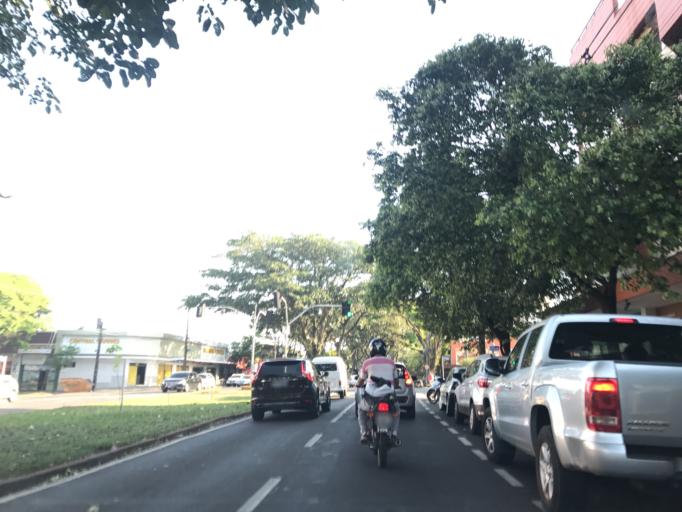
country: BR
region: Parana
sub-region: Maringa
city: Maringa
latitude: -23.4323
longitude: -51.9534
